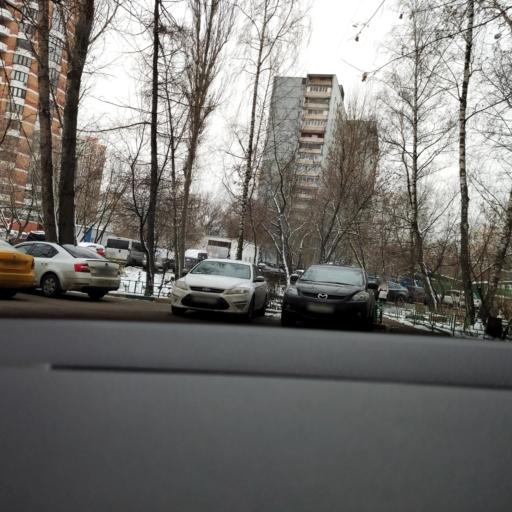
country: RU
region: Moskovskaya
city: Vostryakovo
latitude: 55.6742
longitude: 37.4534
